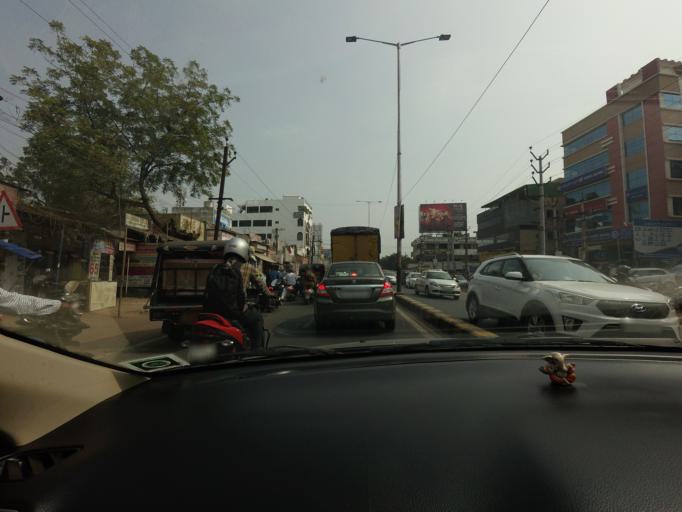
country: IN
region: Andhra Pradesh
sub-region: Krishna
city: Yanamalakuduru
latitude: 16.4902
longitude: 80.6718
